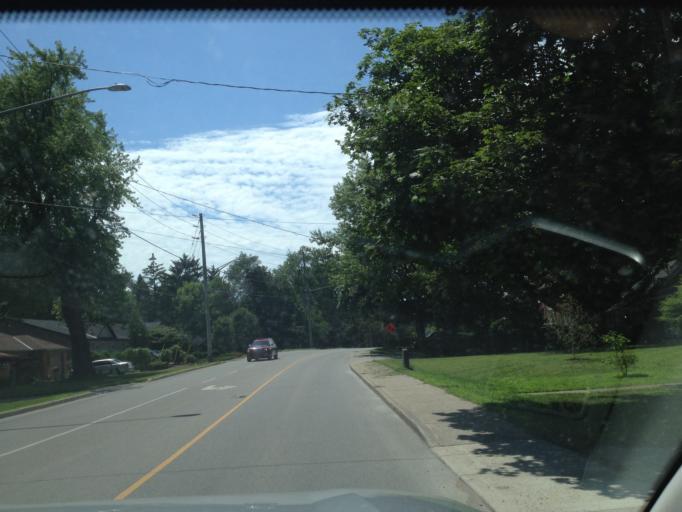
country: CA
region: Ontario
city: London
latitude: 42.9803
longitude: -81.2779
